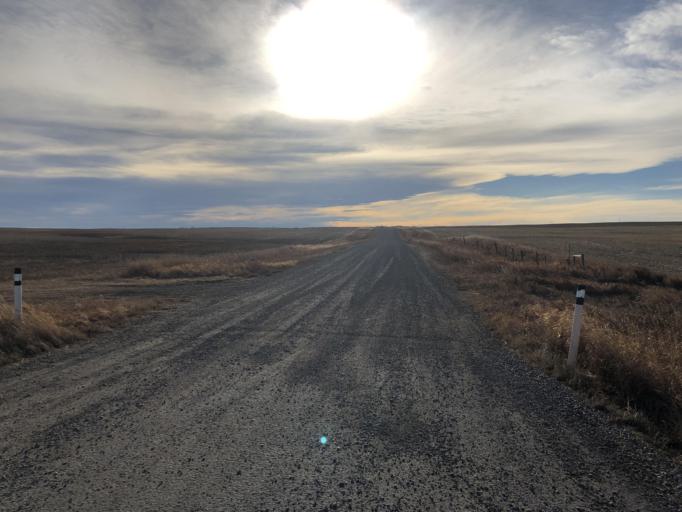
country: CA
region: Alberta
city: Strathmore
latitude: 50.7177
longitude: -113.5135
